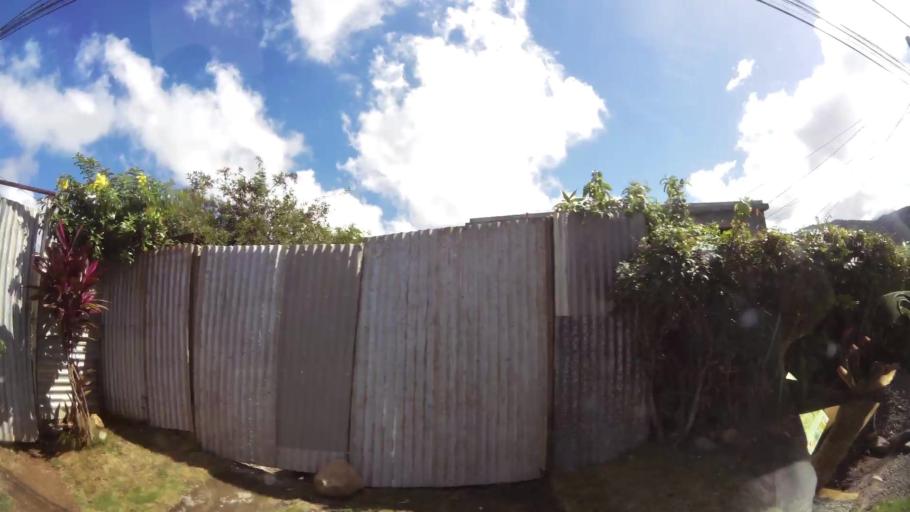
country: DM
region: Saint John
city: Portsmouth
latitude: 15.5771
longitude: -61.4512
